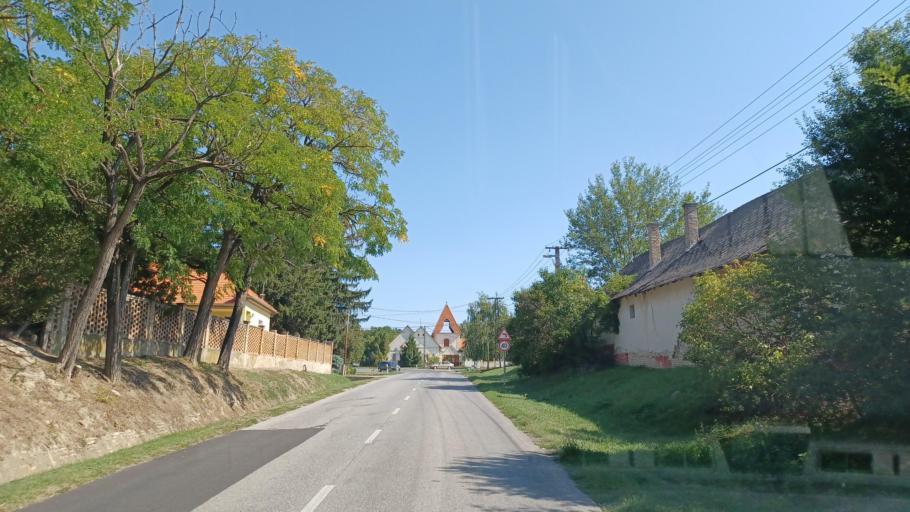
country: HU
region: Tolna
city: Nagydorog
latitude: 46.6749
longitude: 18.6663
